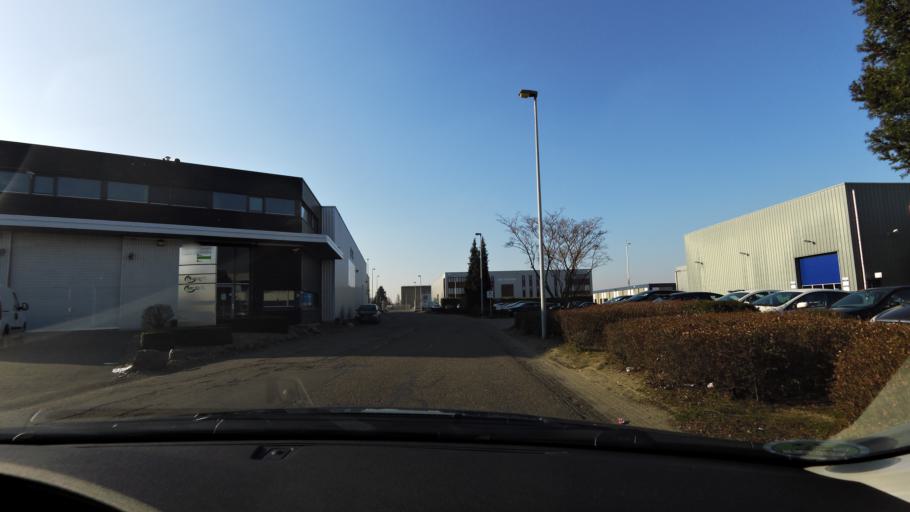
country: NL
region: Limburg
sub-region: Gemeente Beek
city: Beek
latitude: 50.9205
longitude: 5.7841
